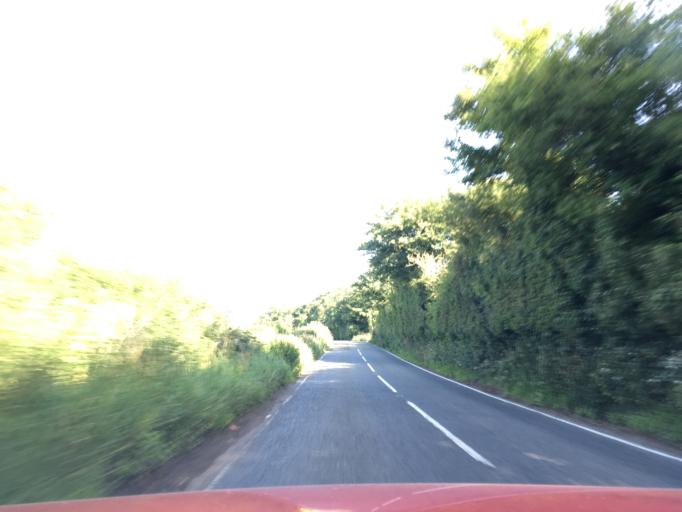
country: GB
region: England
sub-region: South Gloucestershire
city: Bitton
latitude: 51.4398
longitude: -2.4124
